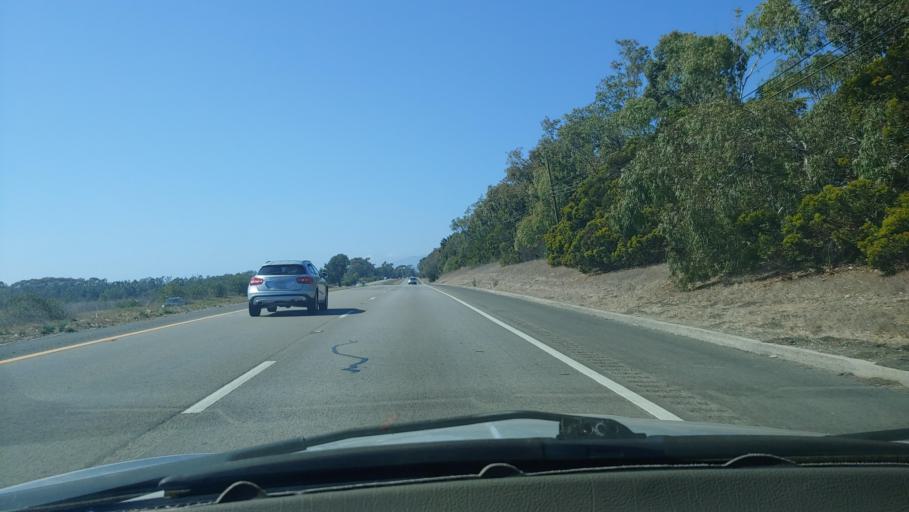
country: US
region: California
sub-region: Santa Barbara County
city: Isla Vista
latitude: 34.4404
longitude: -119.9410
